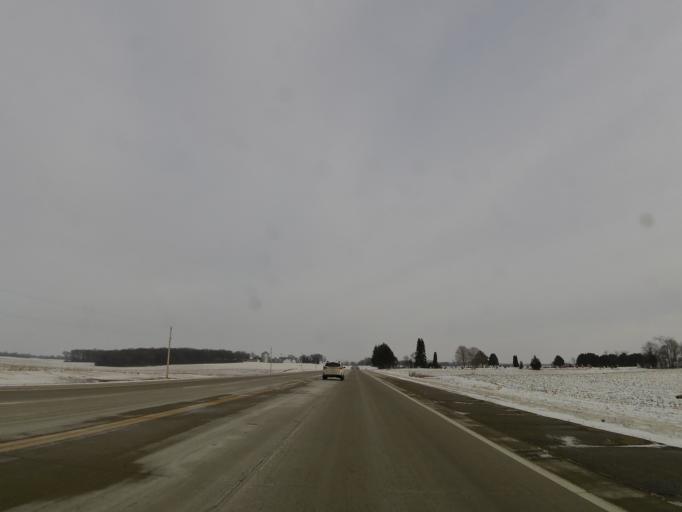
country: US
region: Minnesota
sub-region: McLeod County
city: Hutchinson
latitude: 44.8926
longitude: -94.2464
